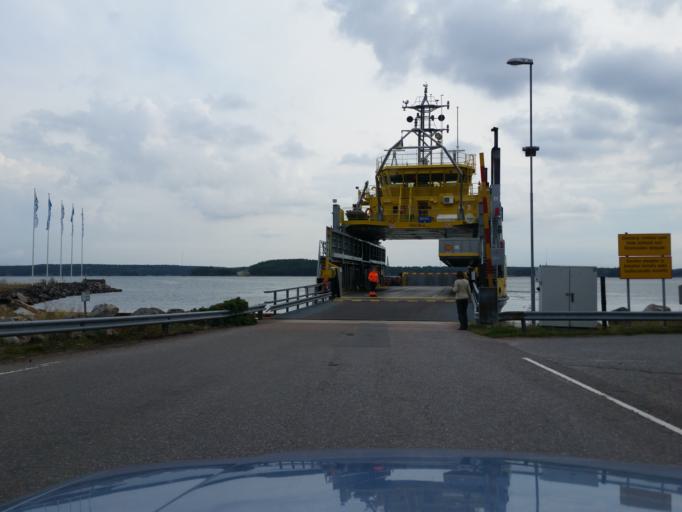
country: FI
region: Varsinais-Suomi
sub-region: Aboland-Turunmaa
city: Nagu
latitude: 60.2224
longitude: 22.0977
